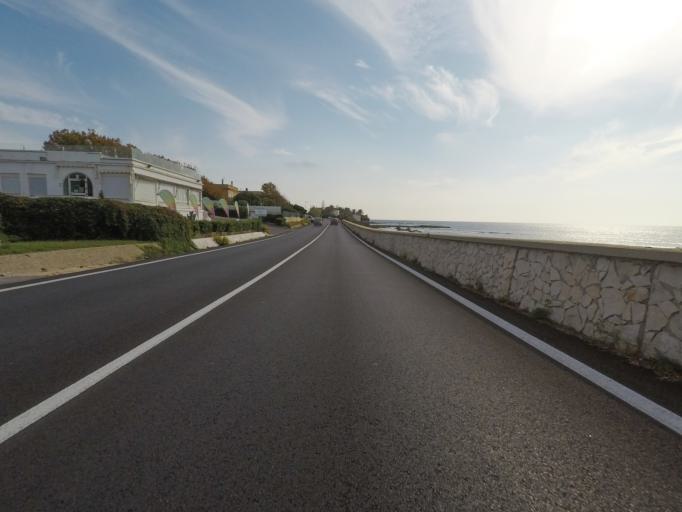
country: IT
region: Latium
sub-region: Citta metropolitana di Roma Capitale
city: Civitavecchia
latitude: 42.0524
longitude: 11.8203
